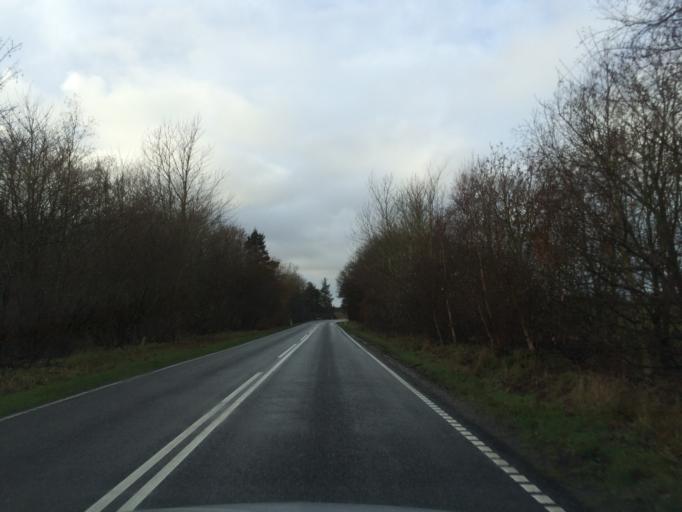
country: DK
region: Central Jutland
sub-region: Holstebro Kommune
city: Ulfborg
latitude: 56.1943
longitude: 8.3299
